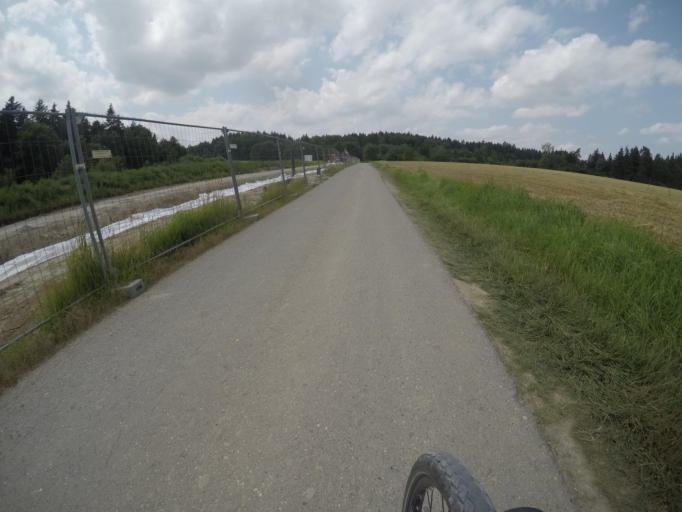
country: DE
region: Baden-Wuerttemberg
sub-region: Freiburg Region
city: Rottweil
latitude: 48.1854
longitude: 8.6108
